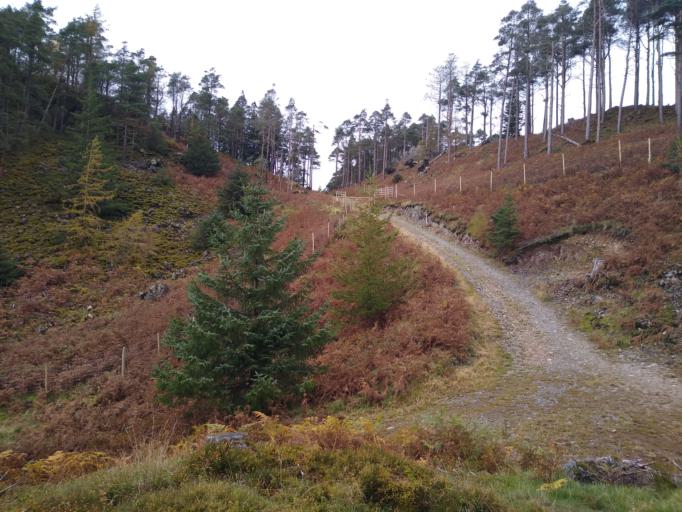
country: GB
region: England
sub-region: Cumbria
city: Keswick
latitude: 54.5641
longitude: -3.0782
